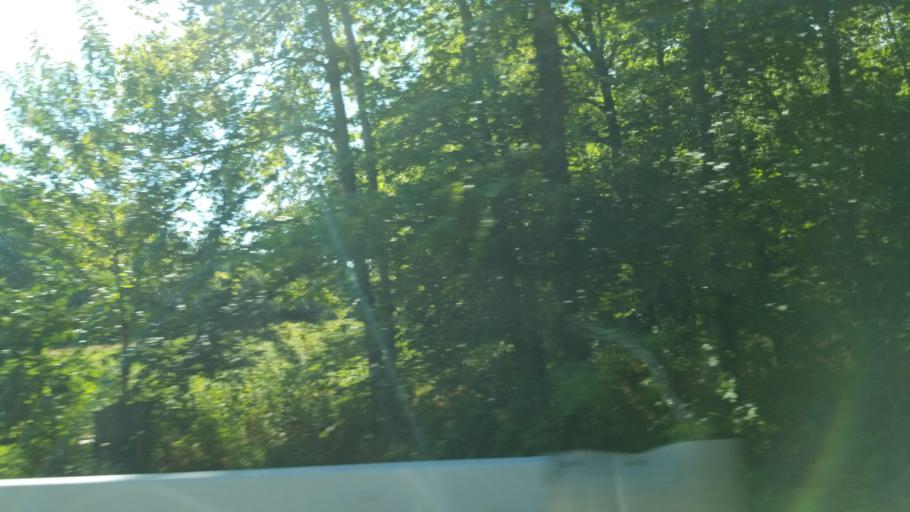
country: US
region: Illinois
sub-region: Saline County
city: Carrier Mills
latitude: 37.7965
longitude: -88.7483
